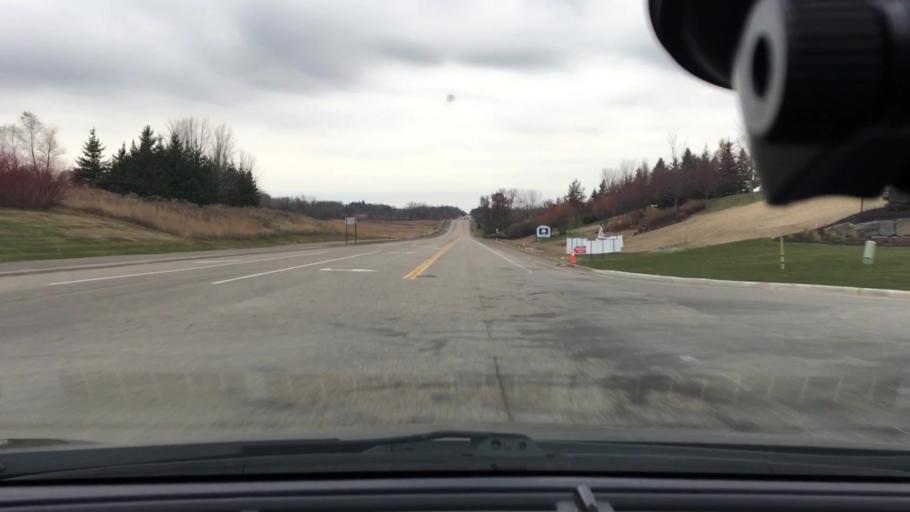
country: US
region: Minnesota
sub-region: Hennepin County
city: Corcoran
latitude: 45.0543
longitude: -93.5221
